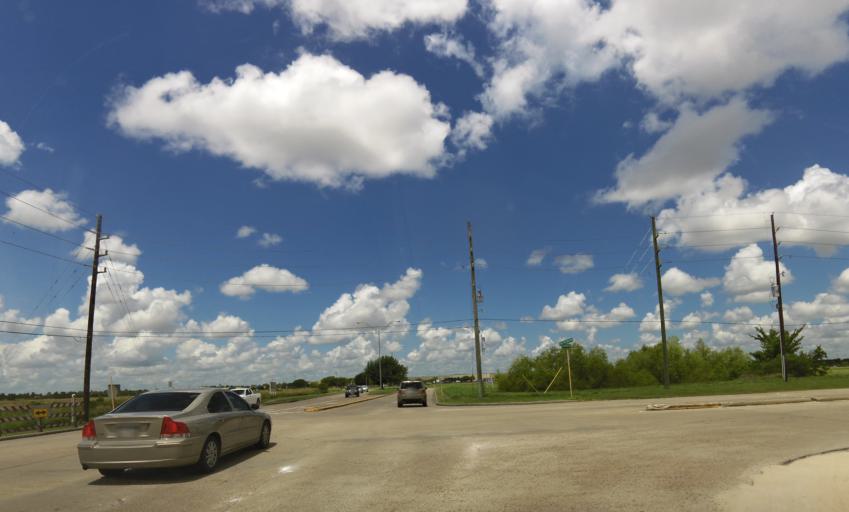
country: US
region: Texas
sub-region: Harris County
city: Katy
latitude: 29.7737
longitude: -95.8015
